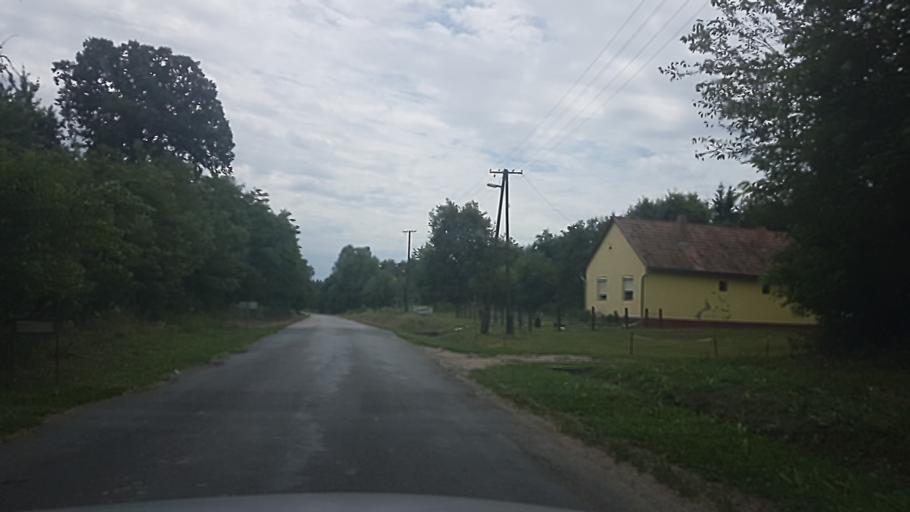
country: HU
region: Somogy
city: Barcs
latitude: 45.9705
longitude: 17.5890
